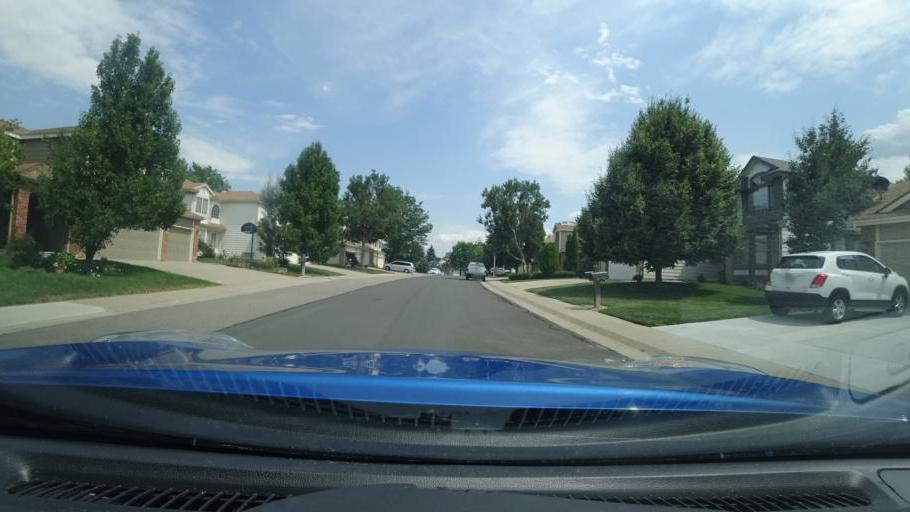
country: US
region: Colorado
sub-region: Adams County
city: Aurora
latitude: 39.6726
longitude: -104.7746
